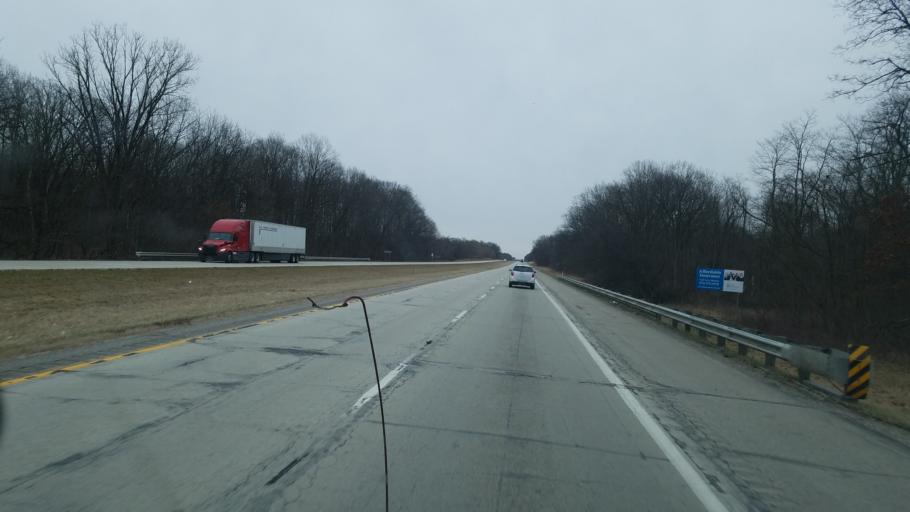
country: US
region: Indiana
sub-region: Starke County
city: Koontz Lake
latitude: 41.3644
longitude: -86.4421
